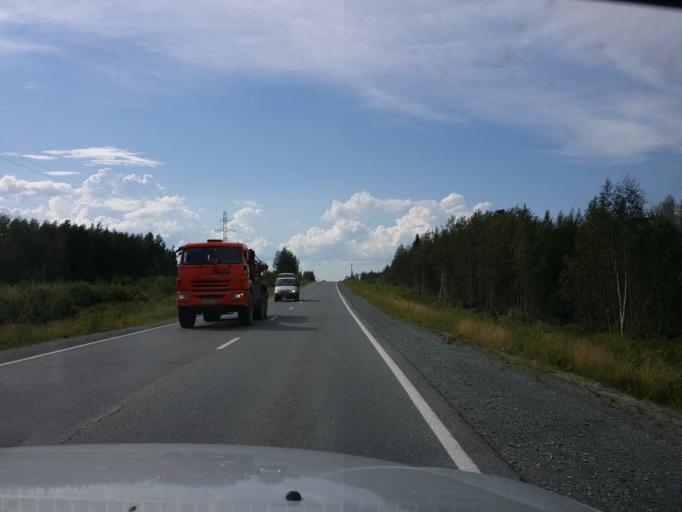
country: RU
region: Khanty-Mansiyskiy Avtonomnyy Okrug
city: Megion
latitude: 61.1024
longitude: 75.9547
